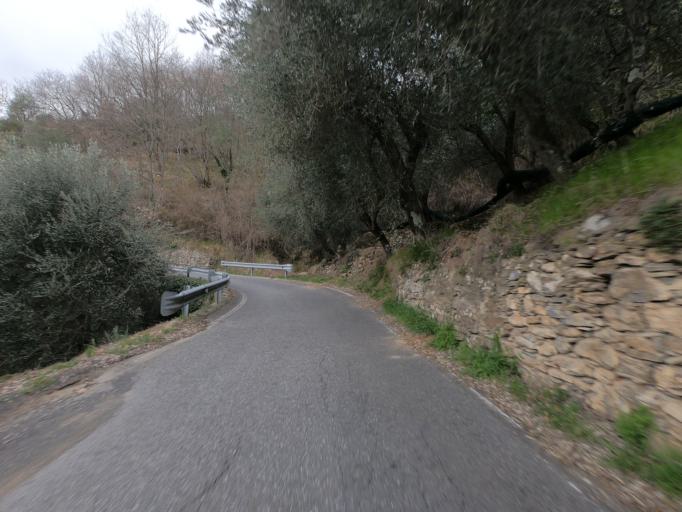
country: IT
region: Liguria
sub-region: Provincia di Savona
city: Testico
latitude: 44.0273
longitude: 8.0112
